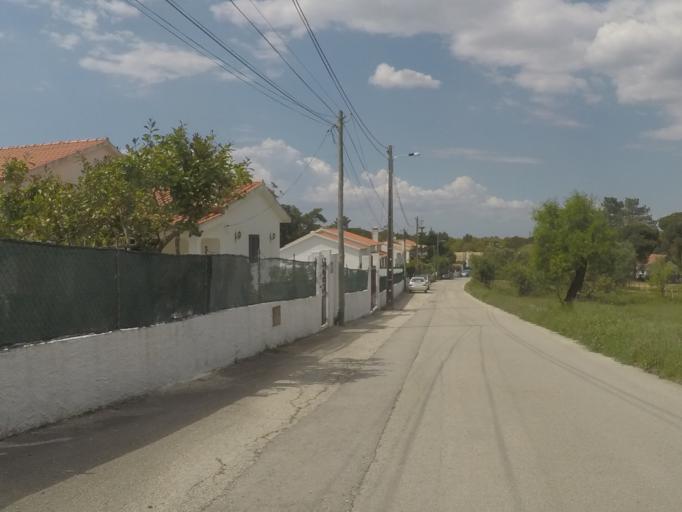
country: PT
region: Setubal
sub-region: Sesimbra
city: Sesimbra
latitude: 38.4612
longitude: -9.0743
